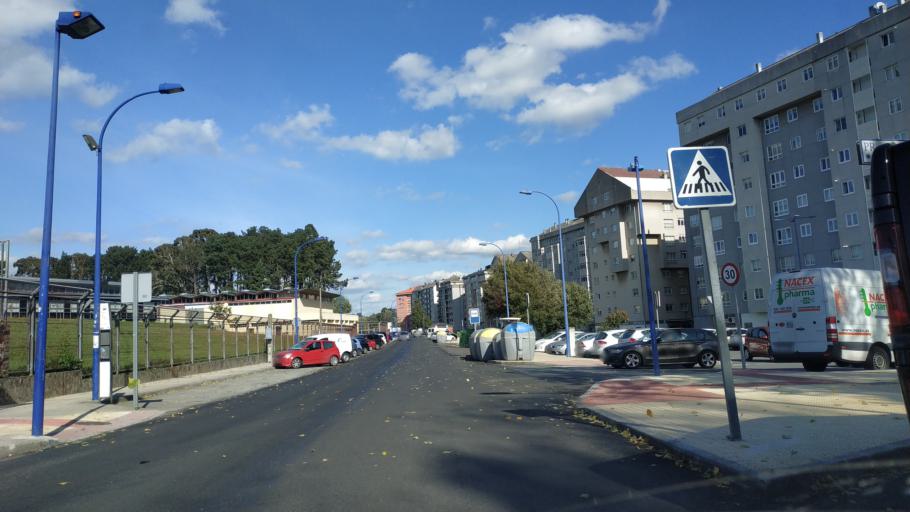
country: ES
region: Galicia
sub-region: Provincia da Coruna
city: Culleredo
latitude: 43.3152
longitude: -8.3745
